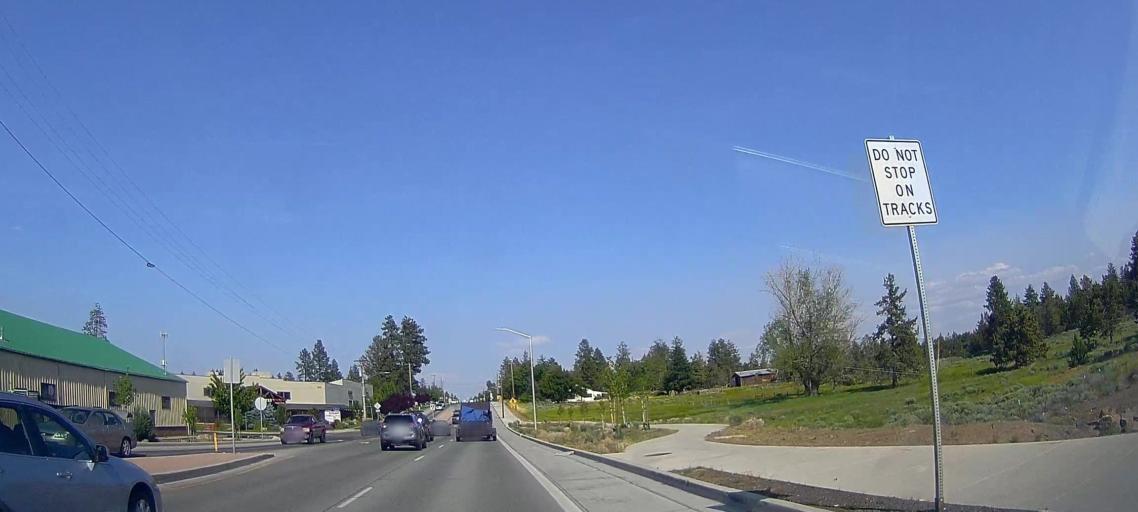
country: US
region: Oregon
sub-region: Deschutes County
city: Bend
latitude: 44.0369
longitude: -121.2888
